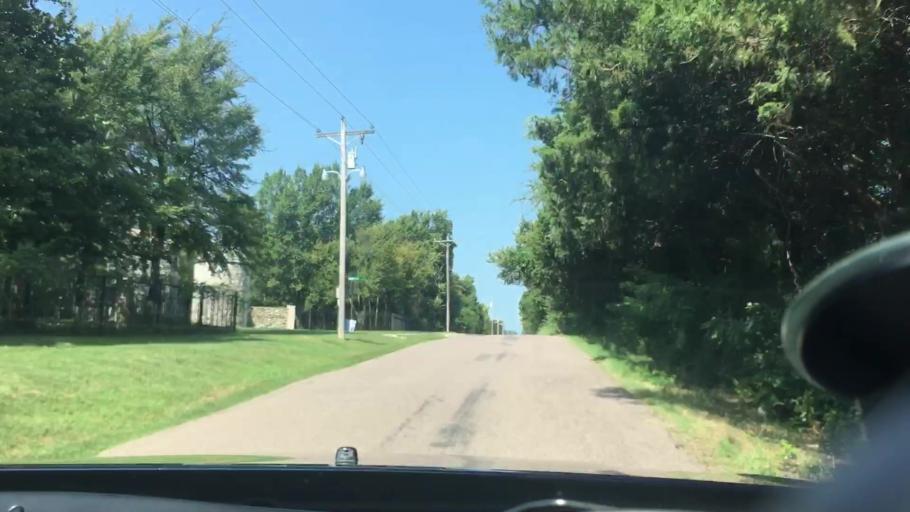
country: US
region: Oklahoma
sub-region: Bryan County
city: Durant
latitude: 34.0267
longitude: -96.4084
